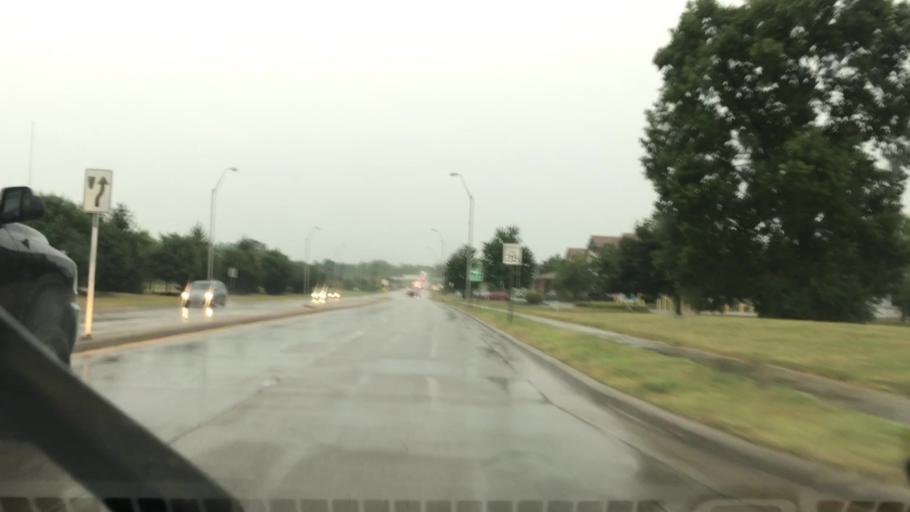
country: US
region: Ohio
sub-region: Greene County
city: Fairborn
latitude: 39.8196
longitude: -84.0083
